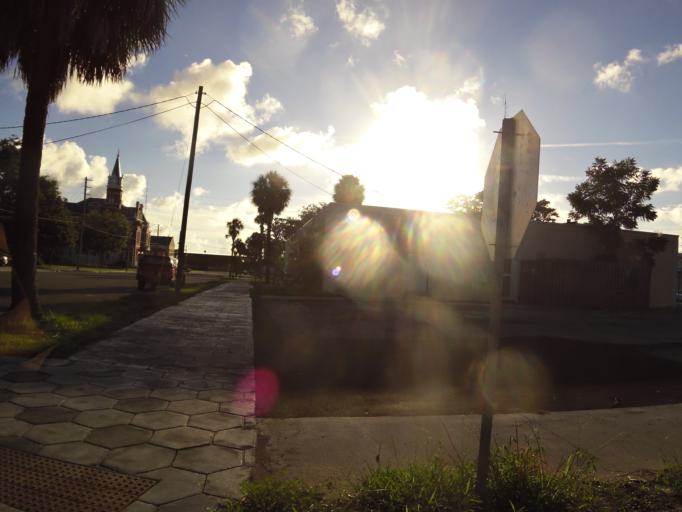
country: US
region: Georgia
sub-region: Glynn County
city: Brunswick
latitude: 31.1468
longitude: -81.4933
